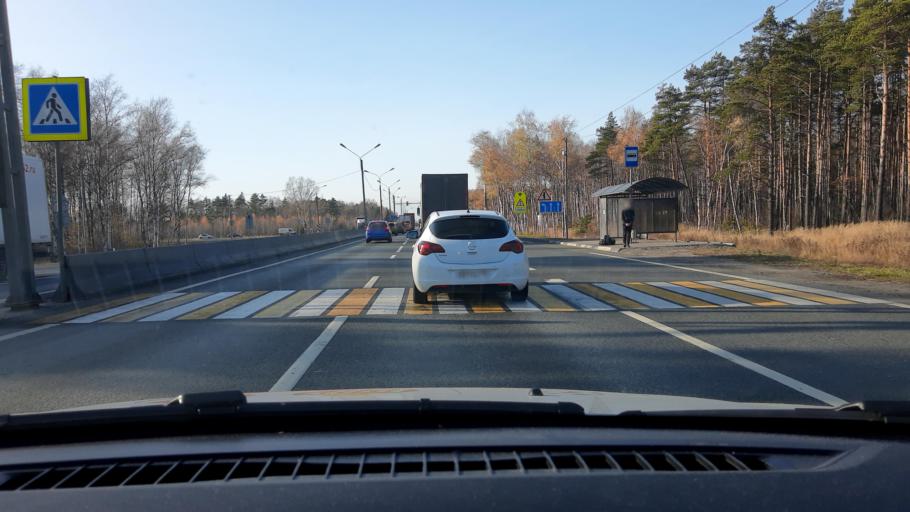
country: RU
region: Nizjnij Novgorod
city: Dzerzhinsk
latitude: 56.2986
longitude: 43.4799
